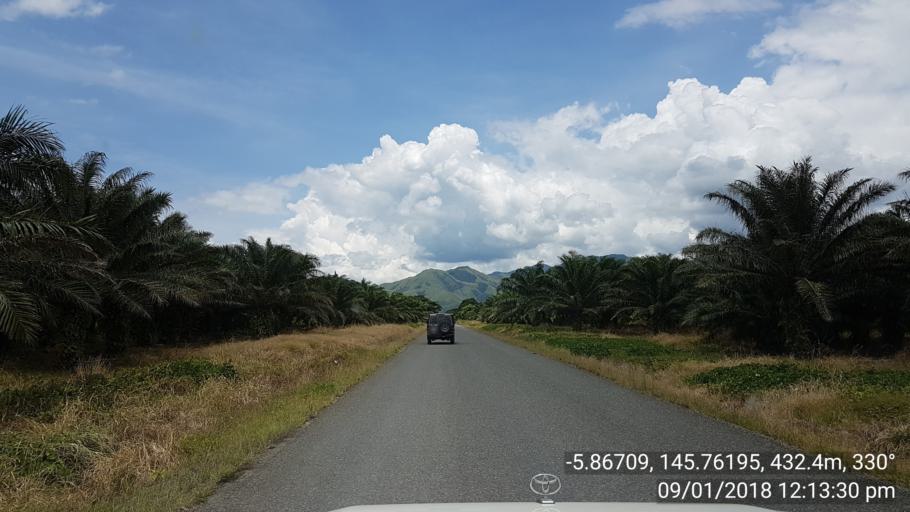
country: PG
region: Eastern Highlands
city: Goroka
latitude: -5.8672
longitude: 145.7620
